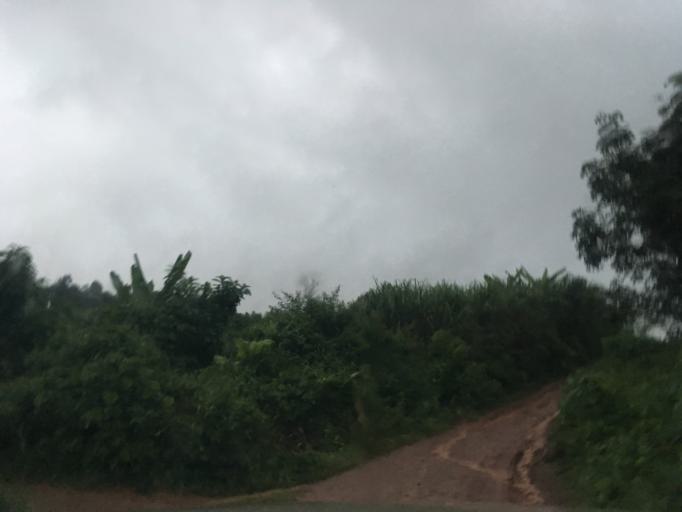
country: LA
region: Oudomxai
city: Muang La
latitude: 21.2524
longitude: 101.9315
